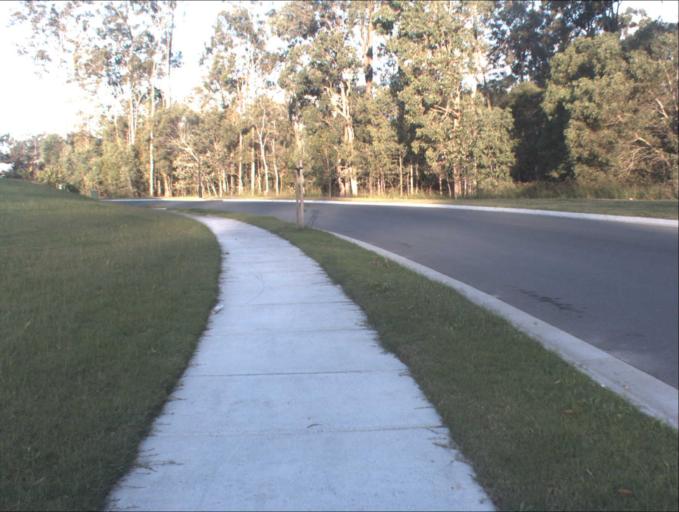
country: AU
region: Queensland
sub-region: Logan
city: North Maclean
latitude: -27.8016
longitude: 152.9560
